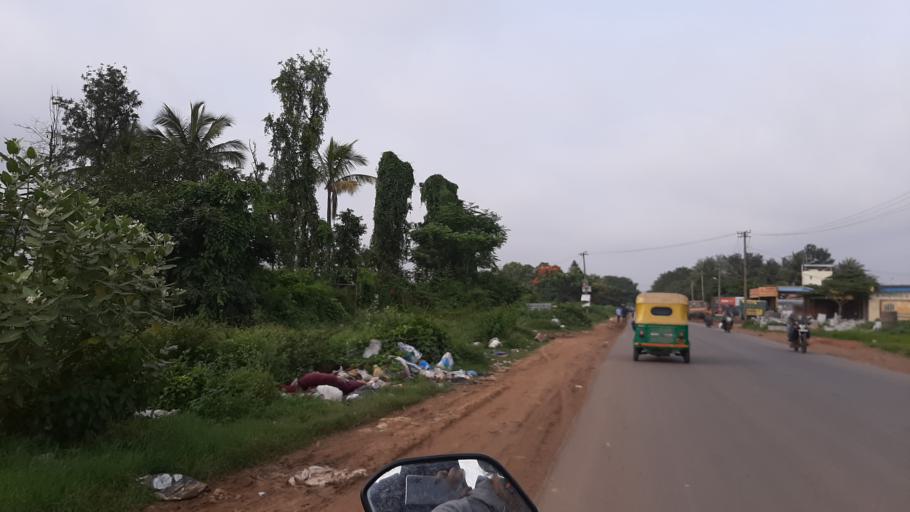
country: IN
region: Karnataka
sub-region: Bangalore Rural
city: Nelamangala
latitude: 12.9825
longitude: 77.4413
